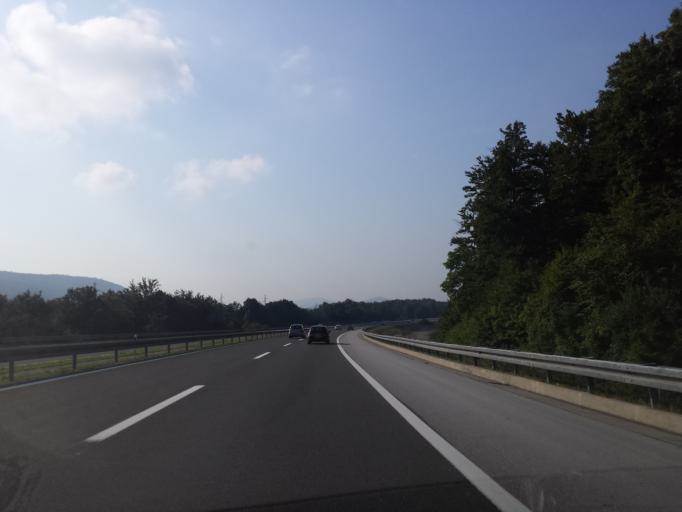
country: HR
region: Karlovacka
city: Ostarije
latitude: 45.2595
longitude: 15.2754
